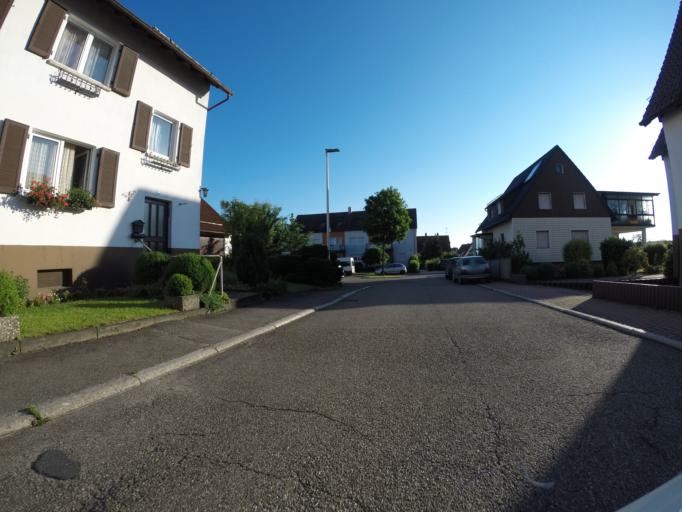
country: DE
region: Baden-Wuerttemberg
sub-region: Karlsruhe Region
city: Dobel
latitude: 48.8552
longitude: 8.5184
